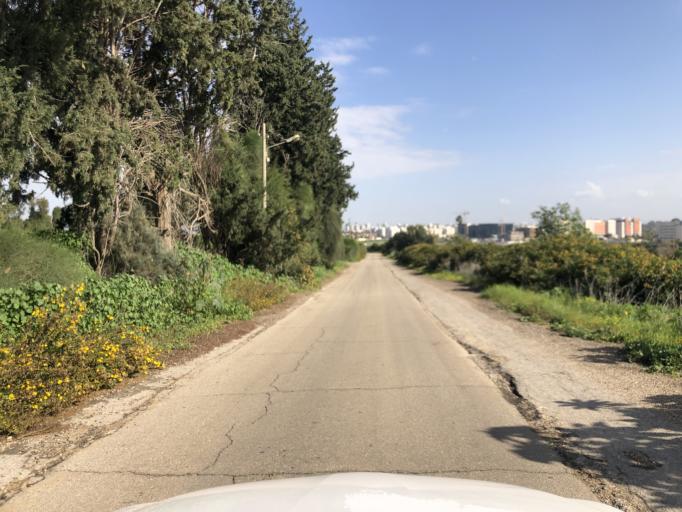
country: IL
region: Central District
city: Ness Ziona
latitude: 31.9143
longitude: 34.7941
